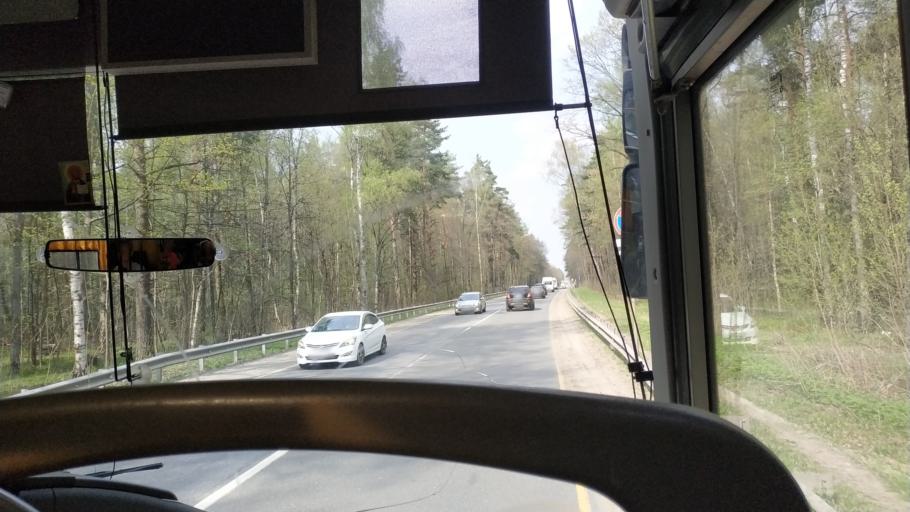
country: RU
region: Moskovskaya
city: Lytkarino
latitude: 55.5994
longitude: 37.9142
